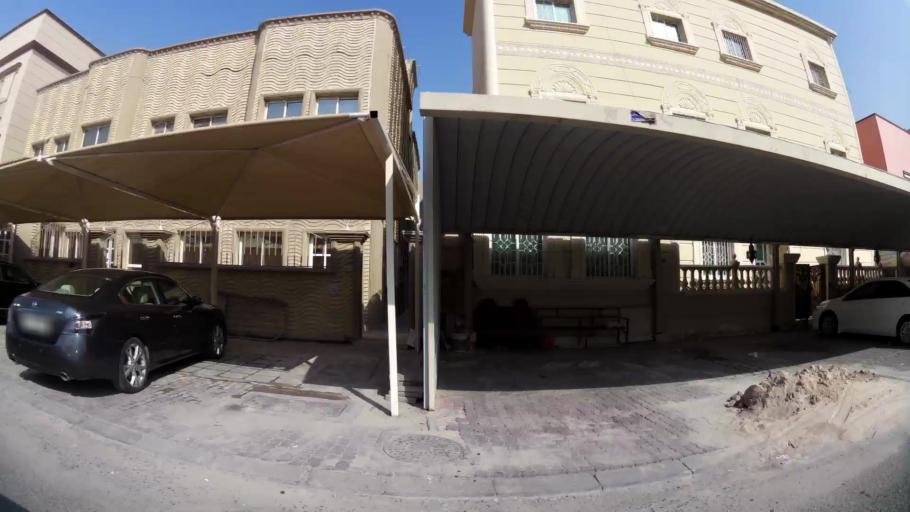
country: KW
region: Al Asimah
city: Ar Rabiyah
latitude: 29.2711
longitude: 47.8895
